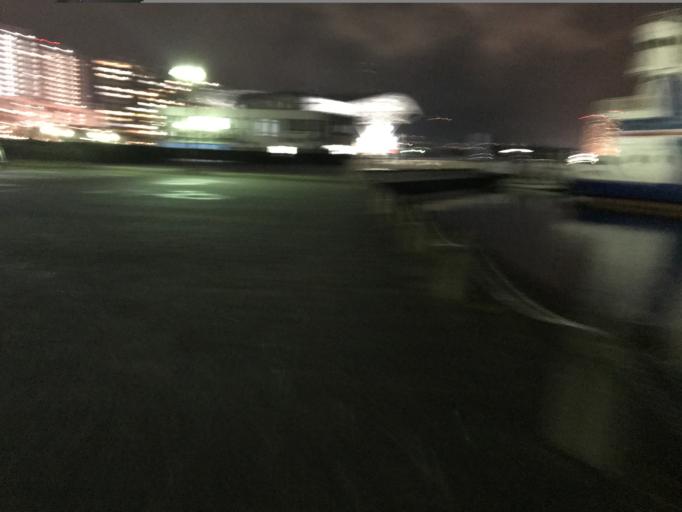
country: JP
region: Shiga Prefecture
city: Otsu-shi
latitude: 35.0119
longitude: 135.8673
